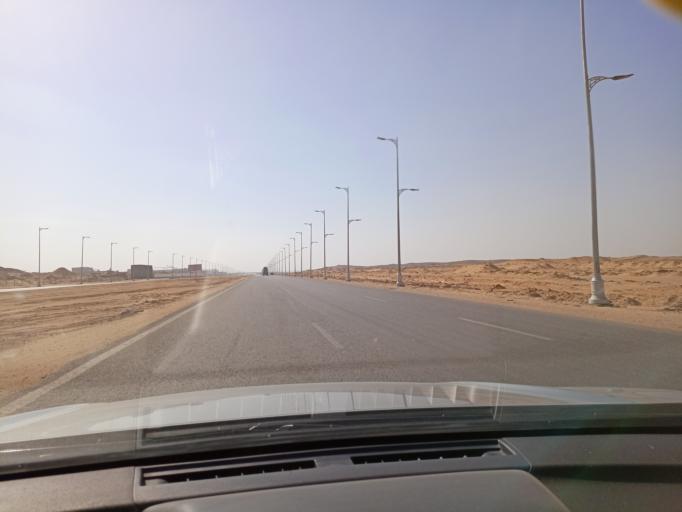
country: EG
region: Muhafazat al Qalyubiyah
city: Al Khankah
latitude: 30.0444
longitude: 31.7112
